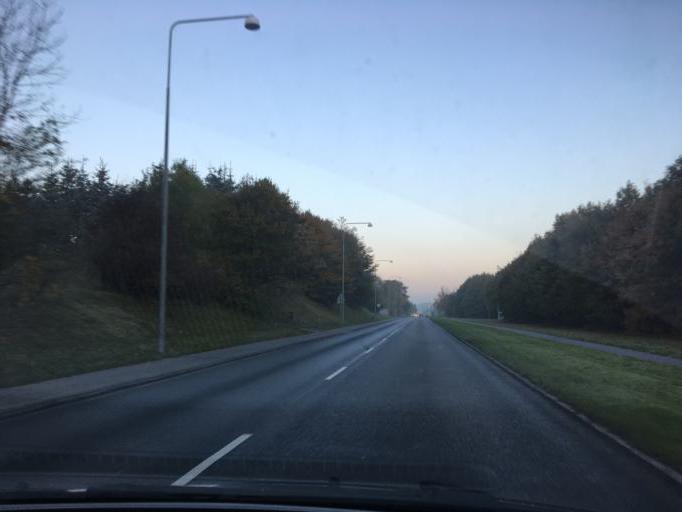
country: DK
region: South Denmark
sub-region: Vejle Kommune
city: Vejle
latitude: 55.6669
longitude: 9.5430
